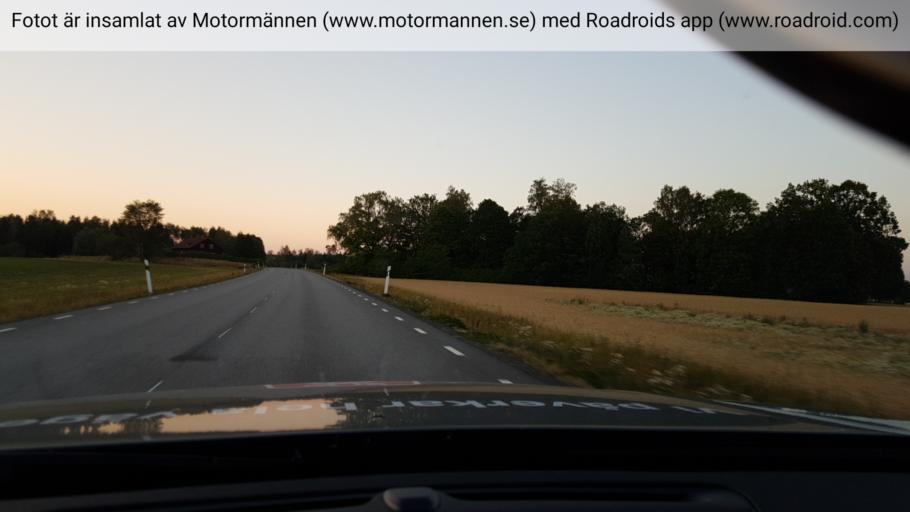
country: SE
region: Uppsala
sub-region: Heby Kommun
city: OEstervala
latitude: 60.1180
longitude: 17.2184
